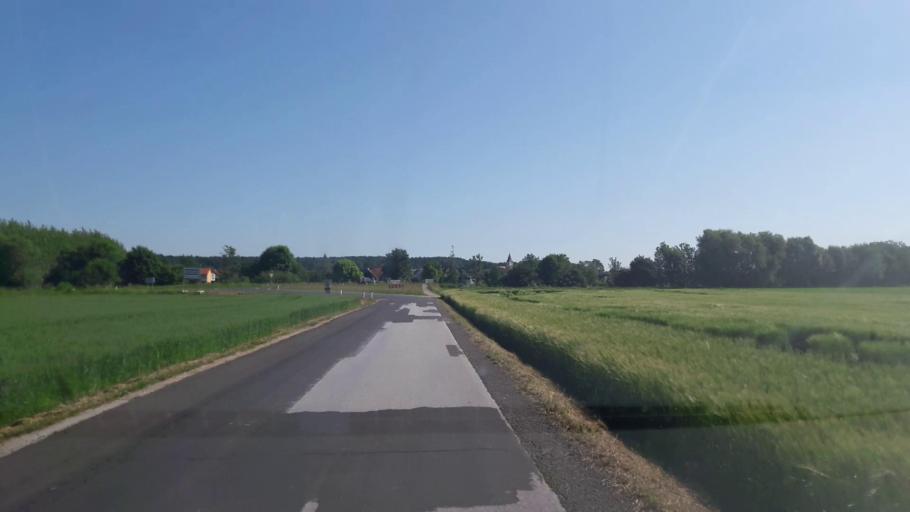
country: AT
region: Styria
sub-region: Politischer Bezirk Hartberg-Fuerstenfeld
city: UEbersbach
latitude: 47.0171
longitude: 16.0500
